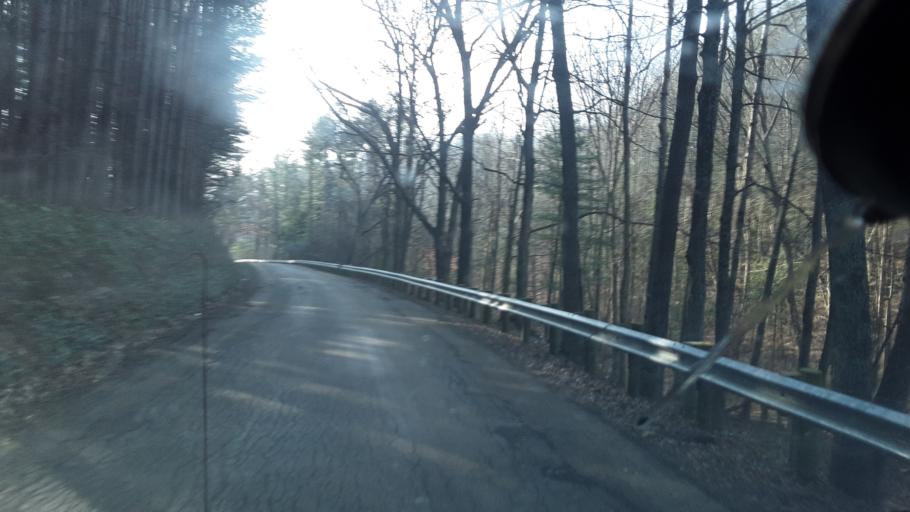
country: US
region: Ohio
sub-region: Knox County
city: Oak Hill
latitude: 40.4183
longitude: -82.2014
